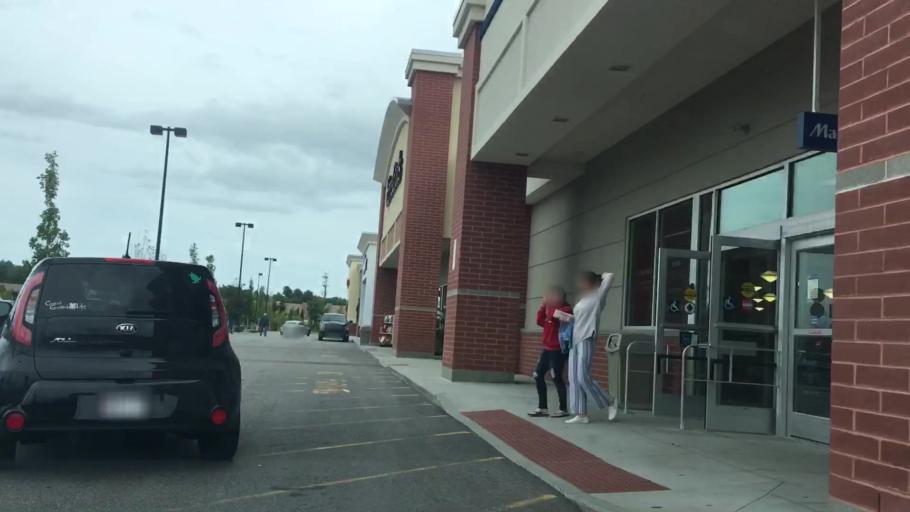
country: US
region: Maine
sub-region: Cumberland County
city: South Portland Gardens
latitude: 43.6230
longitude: -70.3418
